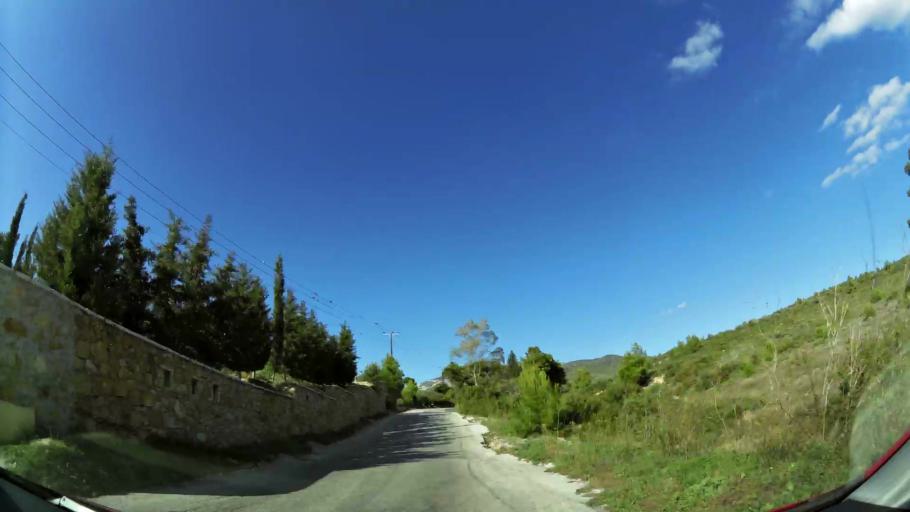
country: GR
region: Attica
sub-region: Nomarchia Anatolikis Attikis
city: Anthousa
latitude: 38.0385
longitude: 23.8822
